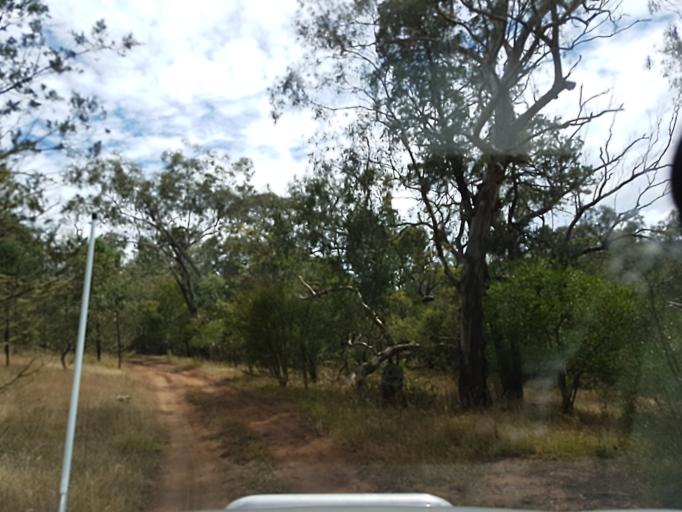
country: AU
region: New South Wales
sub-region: Snowy River
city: Jindabyne
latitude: -36.9433
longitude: 148.3951
